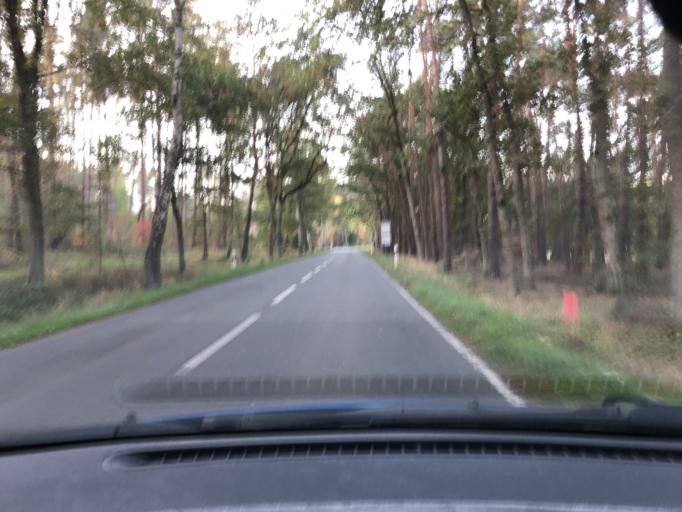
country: DE
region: Lower Saxony
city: Hitzacker
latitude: 53.1343
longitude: 11.0465
